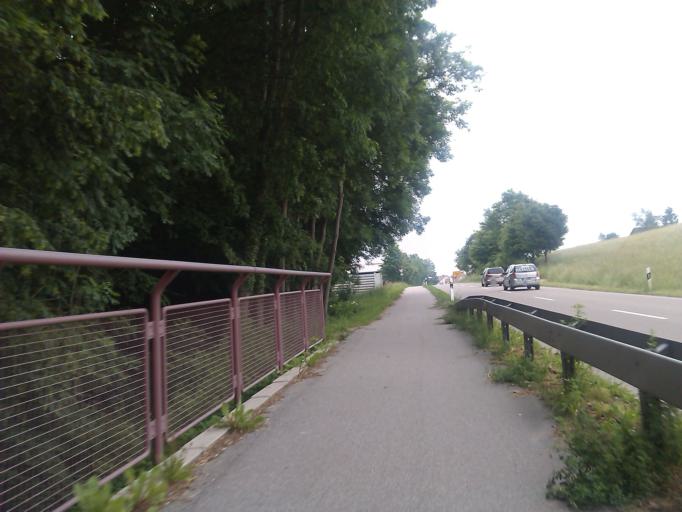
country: DE
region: Baden-Wuerttemberg
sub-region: Regierungsbezirk Stuttgart
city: Mainhardt
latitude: 49.0758
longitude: 9.5421
